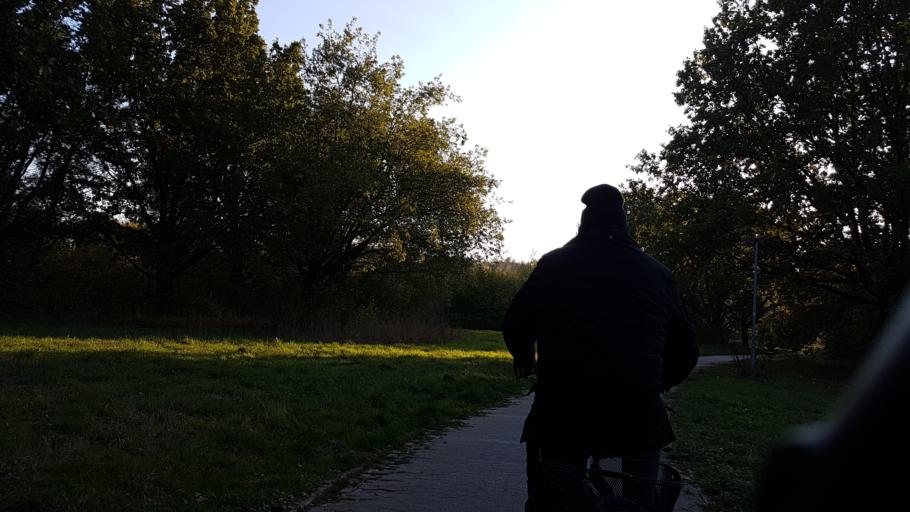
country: DE
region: Lower Saxony
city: Hemmingen
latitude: 52.3255
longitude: 9.7006
